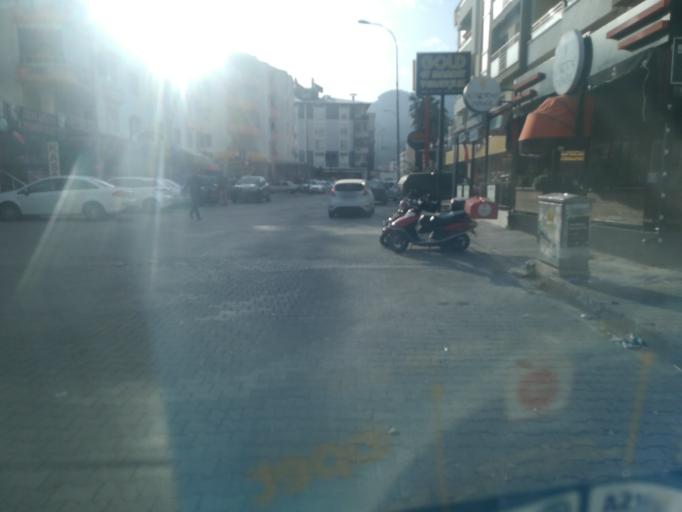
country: TR
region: Osmaniye
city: Osmaniye
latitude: 37.0434
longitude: 36.2269
